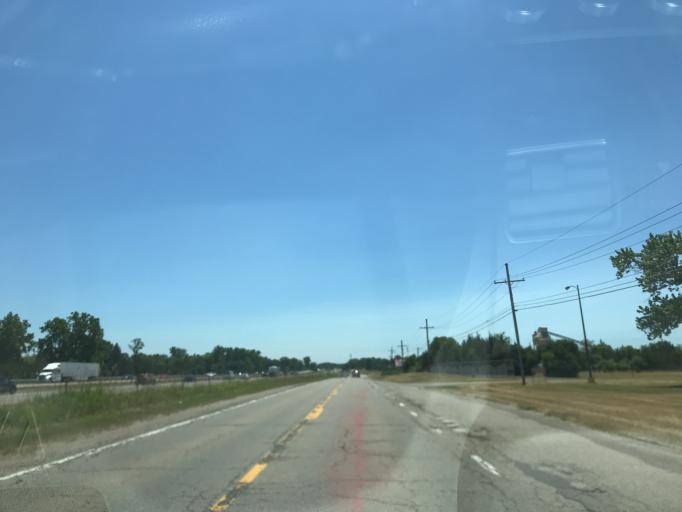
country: US
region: Michigan
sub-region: Livingston County
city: Brighton
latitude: 42.4961
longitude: -83.7581
